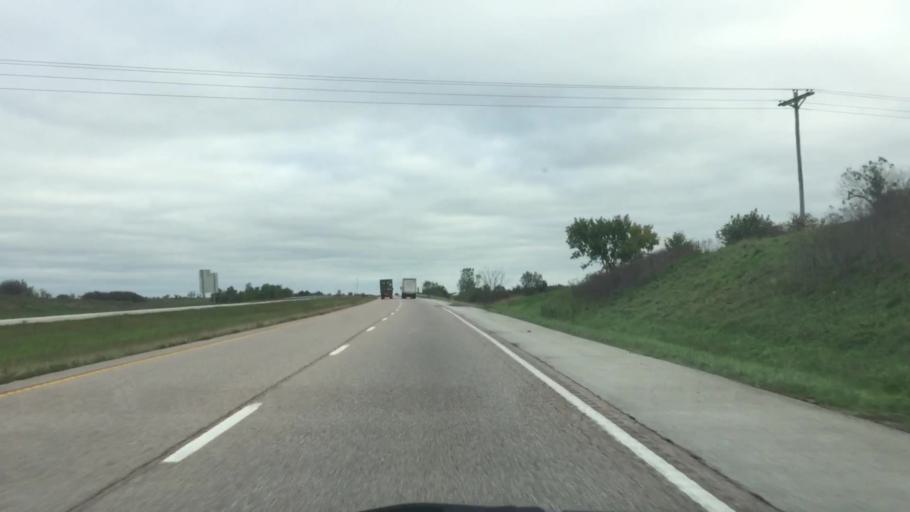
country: US
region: Missouri
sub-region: Clinton County
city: Lathrop
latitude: 39.5714
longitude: -94.2618
